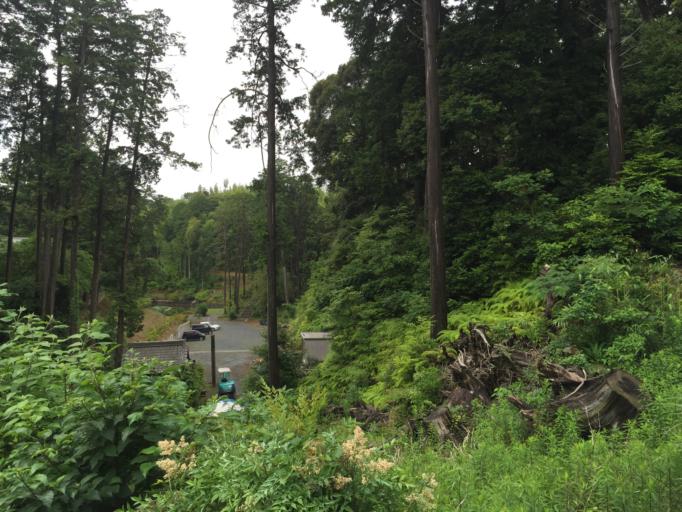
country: JP
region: Shizuoka
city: Fukuroi
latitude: 34.7762
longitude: 137.9203
